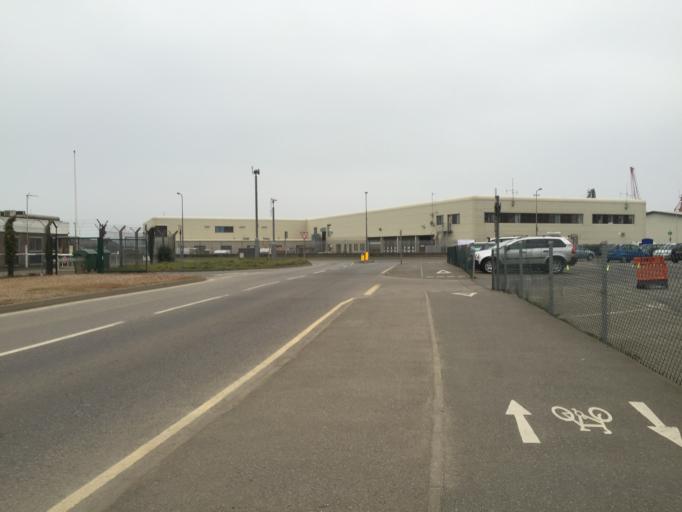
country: JE
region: St Helier
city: Saint Helier
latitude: 49.1741
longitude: -2.1098
